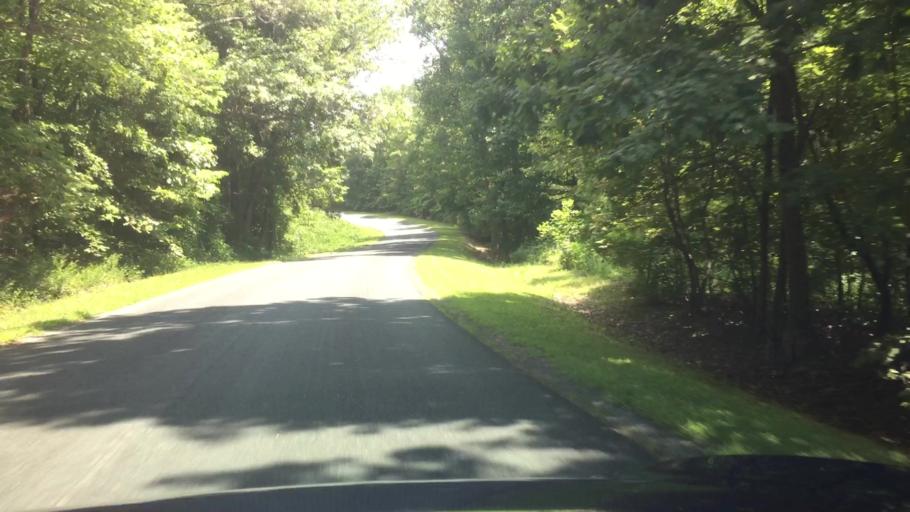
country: US
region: Virginia
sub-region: Appomattox County
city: Appomattox
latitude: 37.3243
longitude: -78.8643
